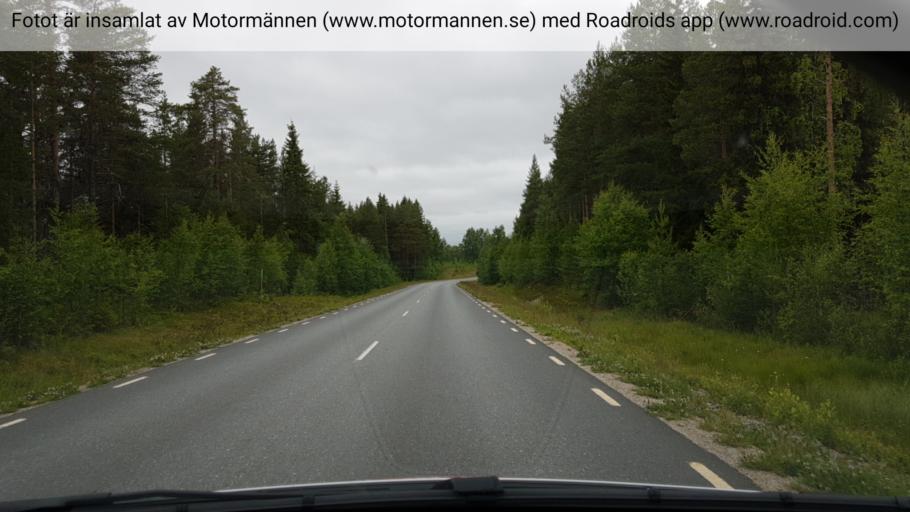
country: SE
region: Vaesterbotten
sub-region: Lycksele Kommun
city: Lycksele
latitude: 64.5069
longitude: 18.9053
